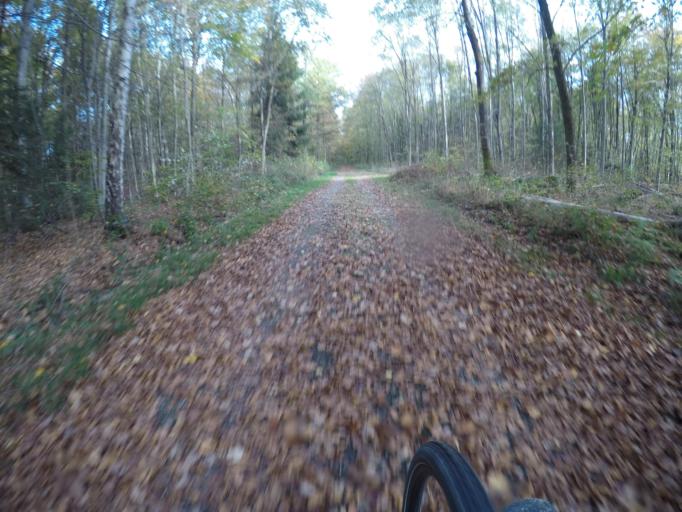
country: DE
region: Baden-Wuerttemberg
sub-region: Regierungsbezirk Stuttgart
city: Sindelfingen
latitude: 48.7330
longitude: 9.0120
